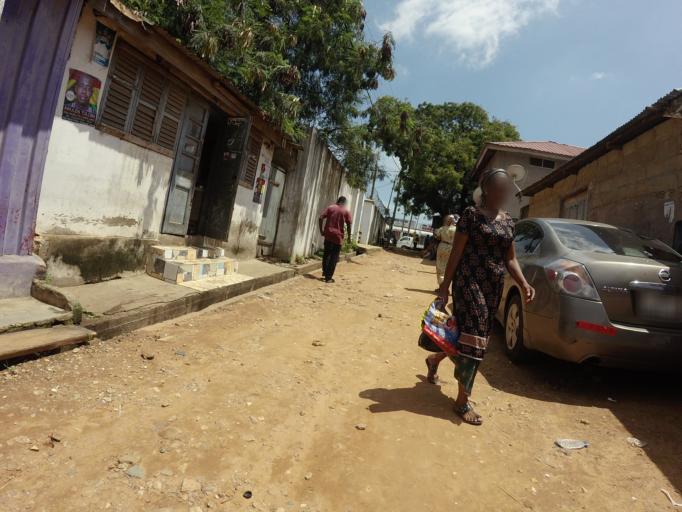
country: GH
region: Greater Accra
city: Accra
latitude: 5.5793
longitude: -0.2005
